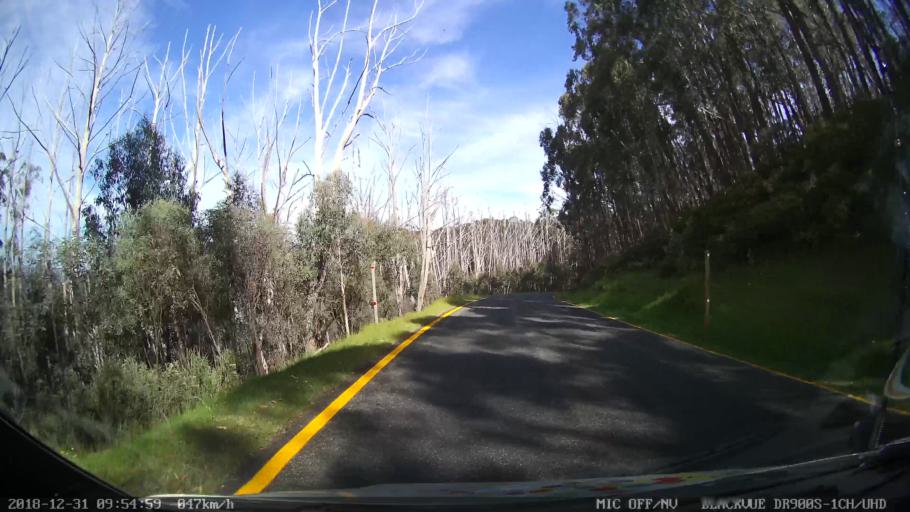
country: AU
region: New South Wales
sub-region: Snowy River
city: Jindabyne
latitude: -36.5330
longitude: 148.2322
